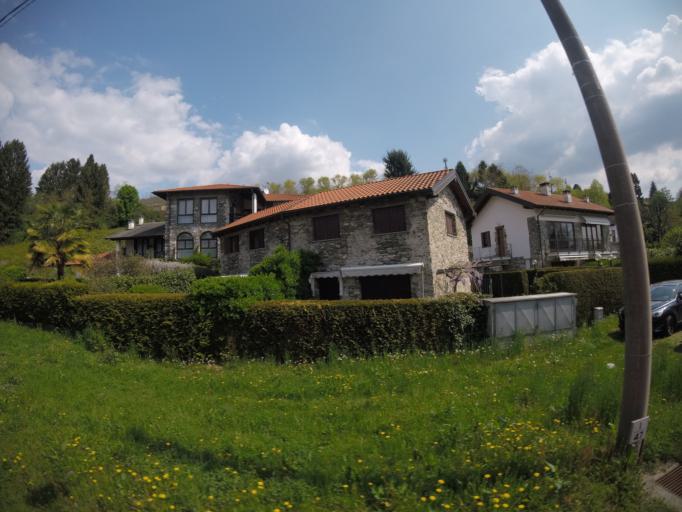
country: IT
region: Piedmont
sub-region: Provincia di Novara
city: Pettenasco
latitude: 45.8203
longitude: 8.4045
